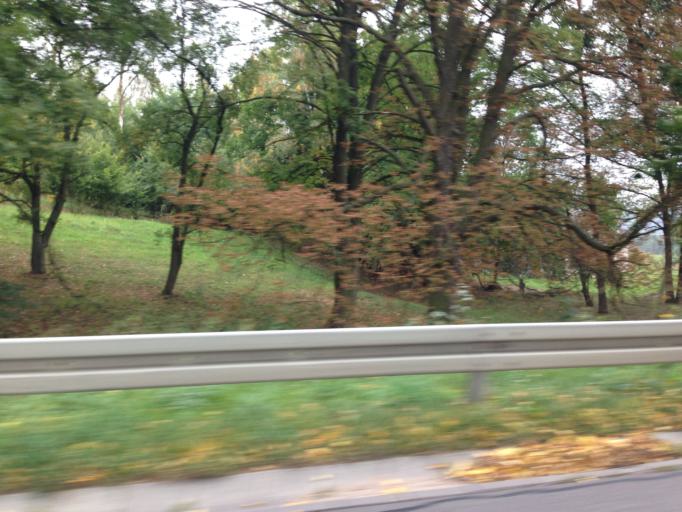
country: PL
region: Kujawsko-Pomorskie
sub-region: Powiat brodnicki
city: Gorzno
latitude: 53.2013
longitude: 19.6404
